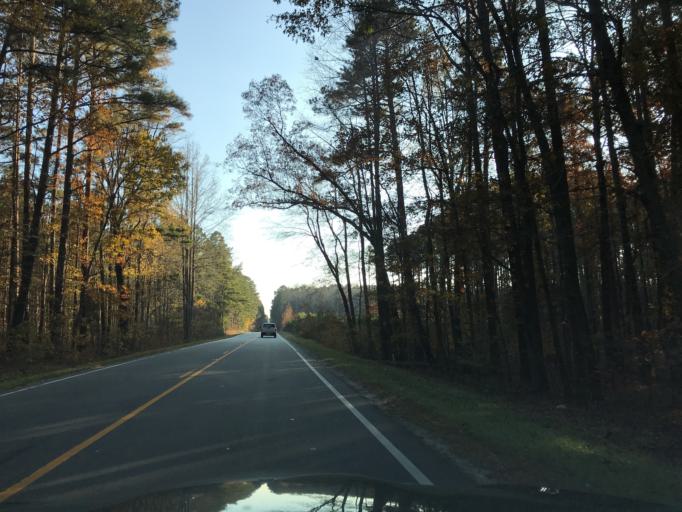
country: US
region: North Carolina
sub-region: Granville County
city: Creedmoor
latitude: 36.0881
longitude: -78.6914
